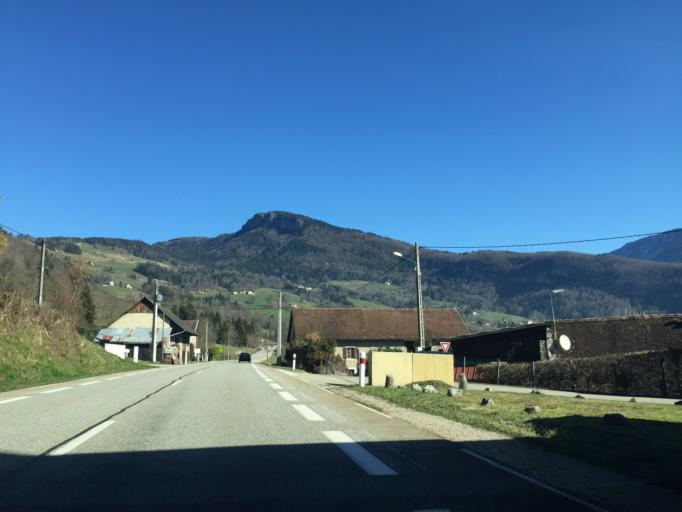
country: FR
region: Rhone-Alpes
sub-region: Departement de la Savoie
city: Les Echelles
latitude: 45.4500
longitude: 5.7666
